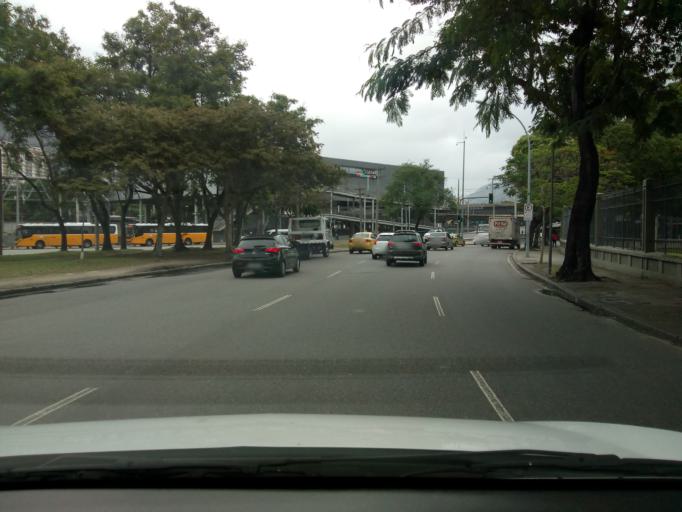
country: BR
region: Rio de Janeiro
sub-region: Rio De Janeiro
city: Rio de Janeiro
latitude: -22.9083
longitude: -43.2222
